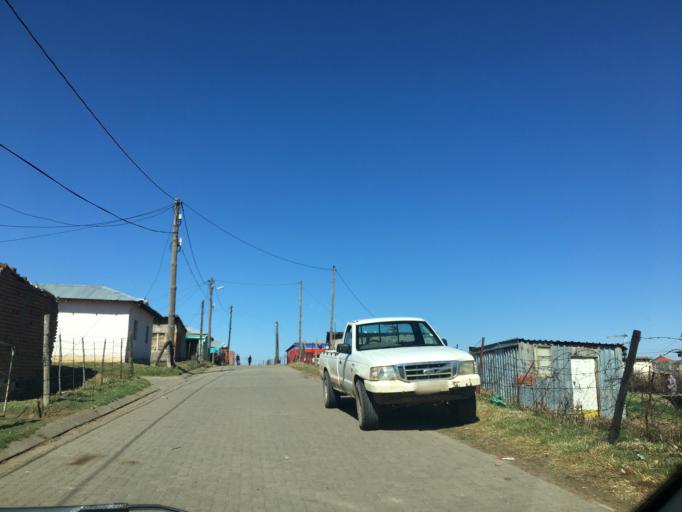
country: ZA
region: Eastern Cape
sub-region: Chris Hani District Municipality
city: Elliot
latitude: -31.3380
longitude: 27.8600
